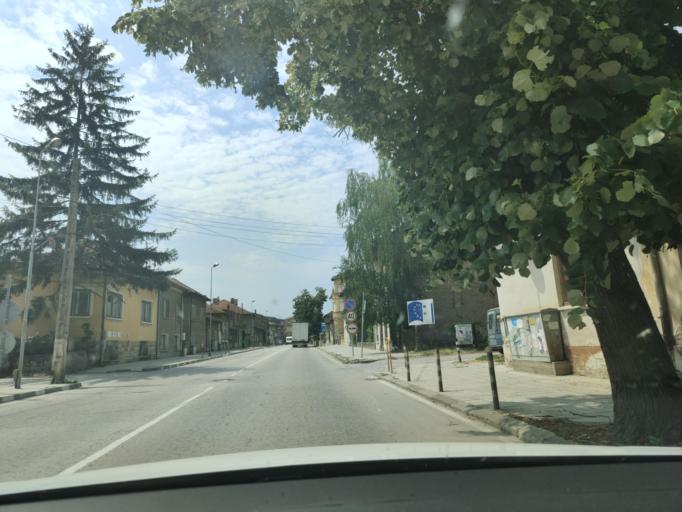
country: BG
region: Vidin
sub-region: Obshtina Dimovo
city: Dimovo
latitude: 43.7426
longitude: 22.7282
